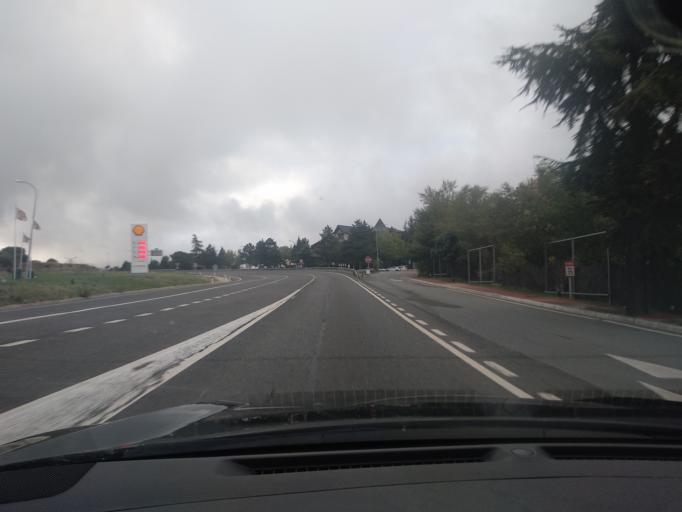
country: ES
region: Castille and Leon
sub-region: Provincia de Segovia
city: Otero de Herreros
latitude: 40.7773
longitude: -4.2086
